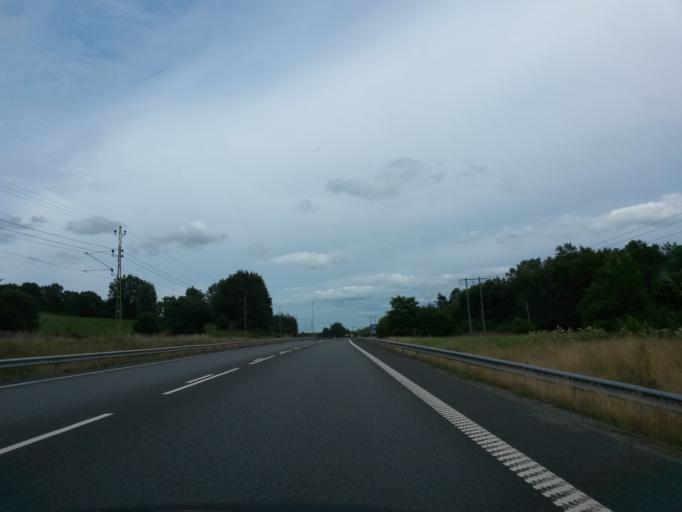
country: SE
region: Vaestra Goetaland
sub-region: Marks Kommun
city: Kinna
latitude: 57.4583
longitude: 12.5858
